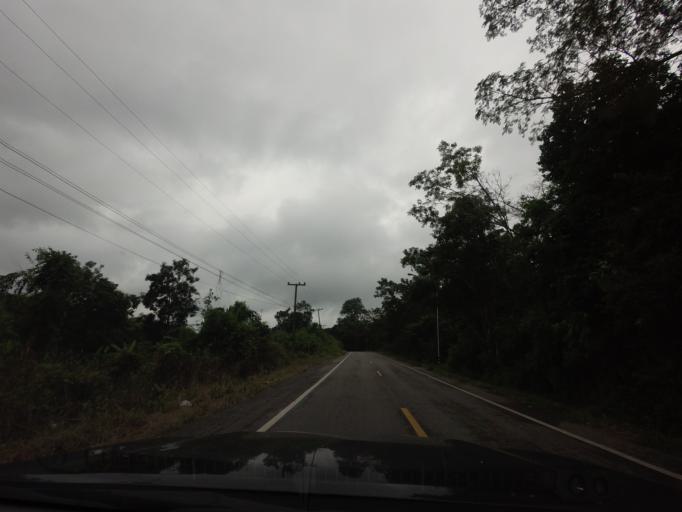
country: TH
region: Nong Khai
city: Sangkhom
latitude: 18.0263
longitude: 102.3573
